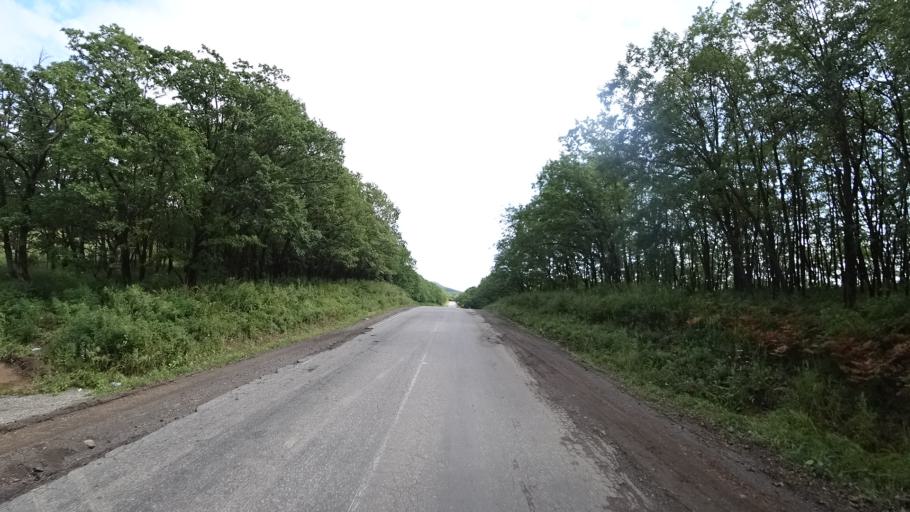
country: RU
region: Primorskiy
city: Lyalichi
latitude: 44.1425
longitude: 132.4048
